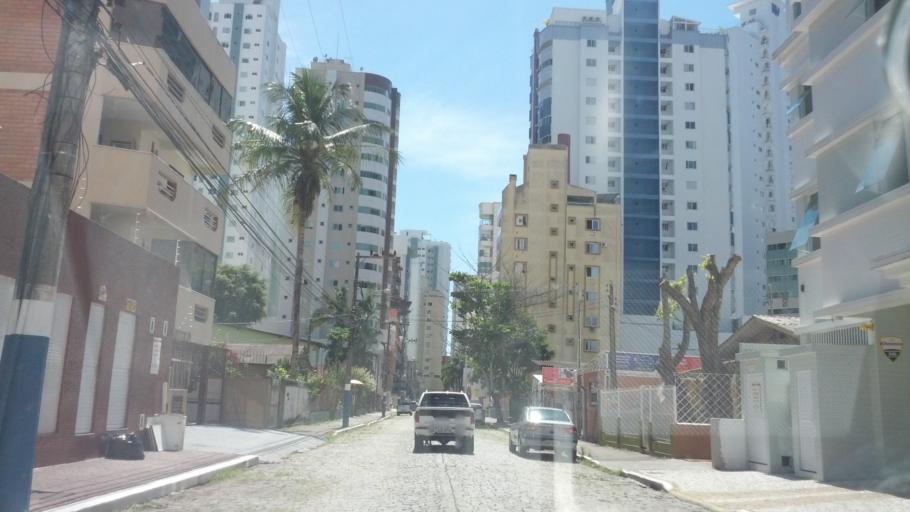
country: BR
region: Santa Catarina
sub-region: Balneario Camboriu
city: Balneario Camboriu
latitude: -26.9998
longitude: -48.6285
